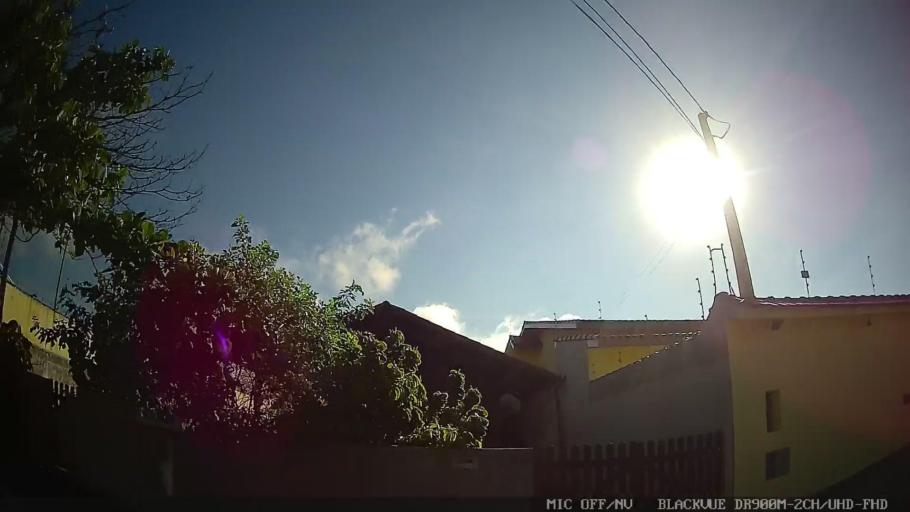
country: BR
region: Sao Paulo
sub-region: Peruibe
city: Peruibe
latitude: -24.2826
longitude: -46.9480
